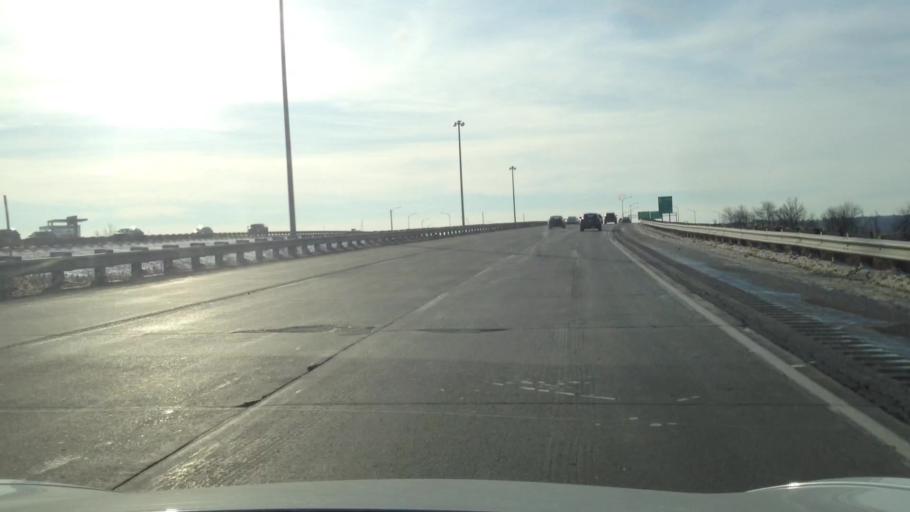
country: CA
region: Quebec
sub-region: Monteregie
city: Vaudreuil-Dorion
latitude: 45.4031
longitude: -74.0521
